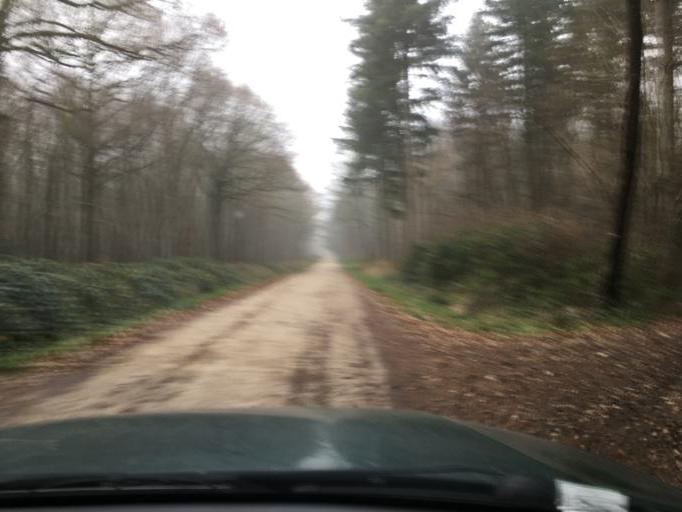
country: FR
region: Centre
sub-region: Departement du Loiret
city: Saran
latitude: 47.9871
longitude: 1.8978
